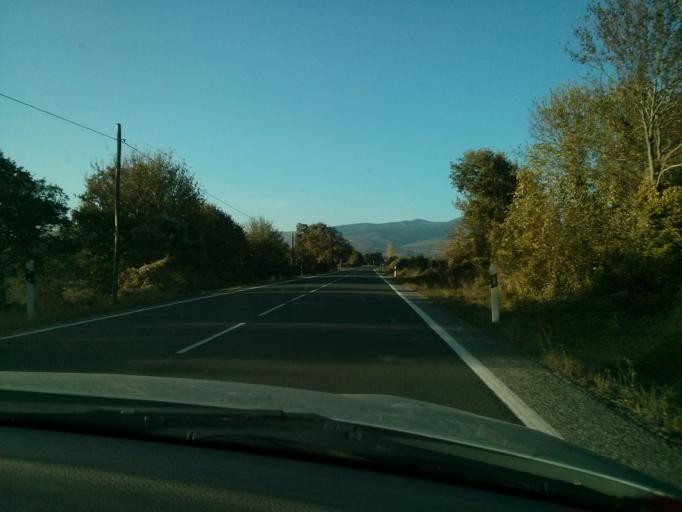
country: ES
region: Castille and Leon
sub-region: Provincia de Burgos
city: Espinosa de los Monteros
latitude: 43.0528
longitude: -3.4896
